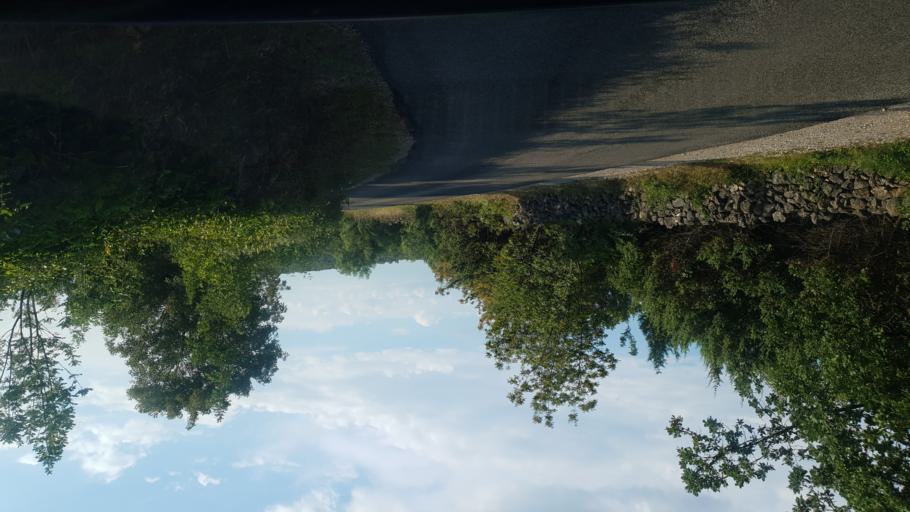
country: HR
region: Primorsko-Goranska
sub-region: Grad Crikvenica
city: Jadranovo
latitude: 45.1733
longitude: 14.6062
